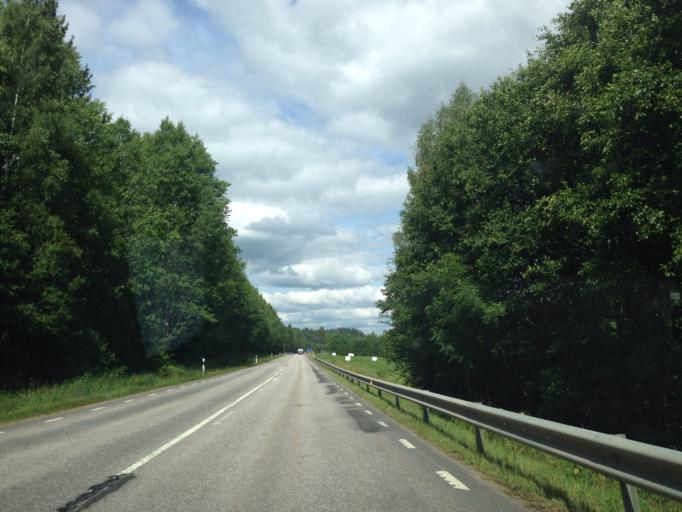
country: SE
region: OEstergoetland
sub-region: Kinda Kommun
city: Kisa
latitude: 57.9701
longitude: 15.6511
